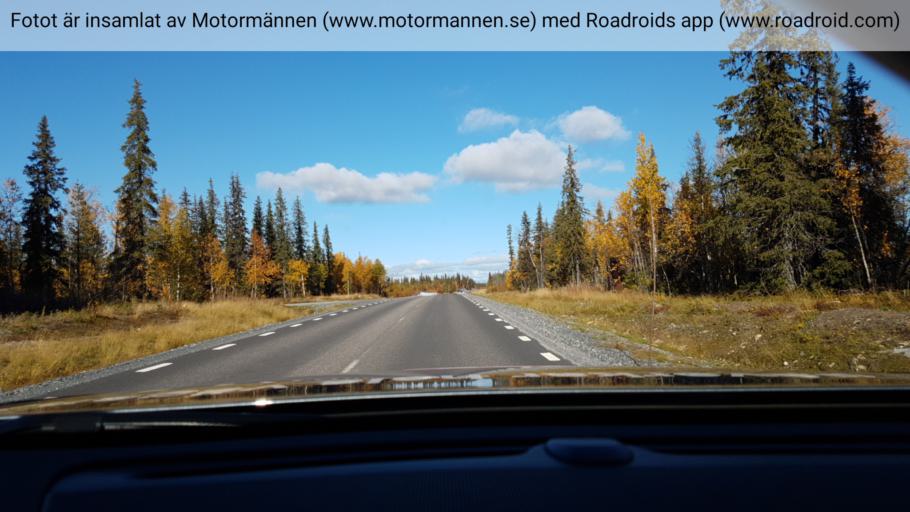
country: SE
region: Norrbotten
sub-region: Gallivare Kommun
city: Gaellivare
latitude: 66.9829
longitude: 20.7422
